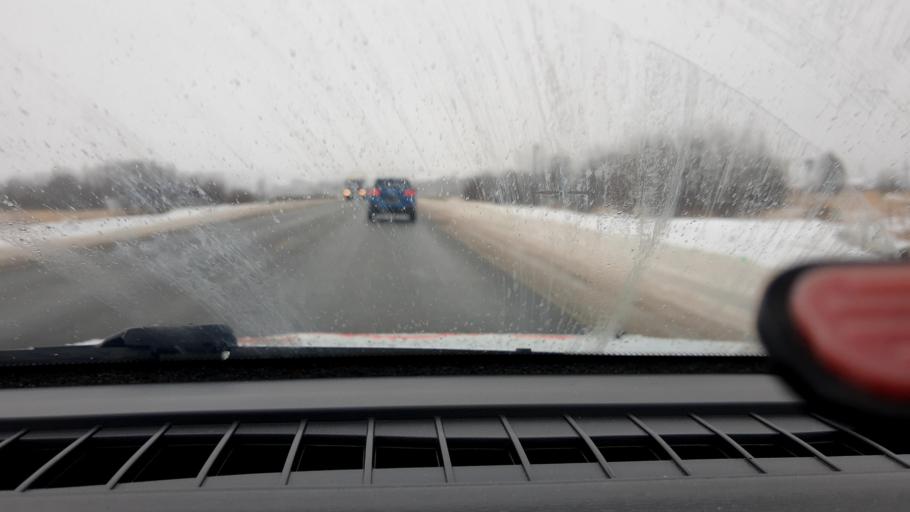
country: RU
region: Nizjnij Novgorod
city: Kstovo
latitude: 56.1139
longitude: 44.1942
